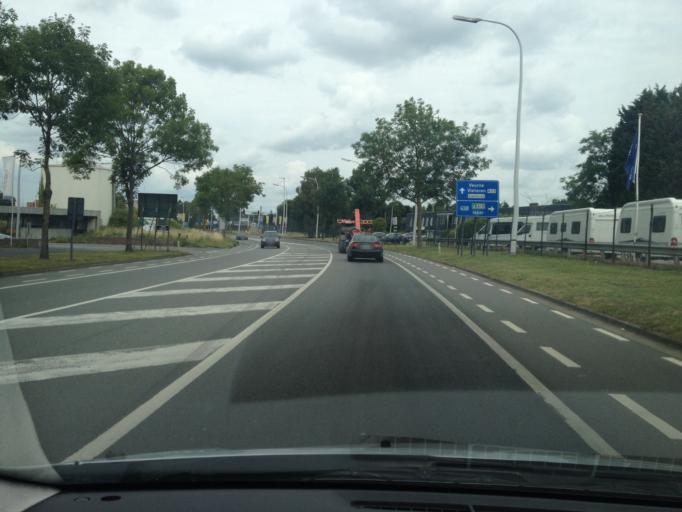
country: BE
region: Flanders
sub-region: Provincie West-Vlaanderen
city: Poperinge
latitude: 50.8522
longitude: 2.7444
